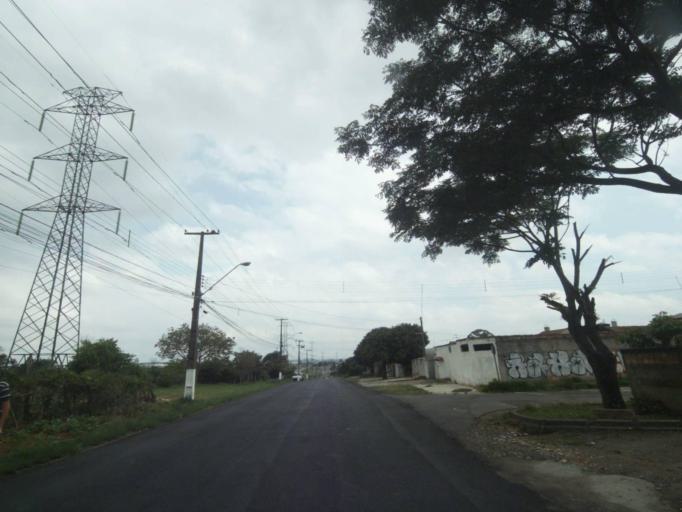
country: BR
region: Parana
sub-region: Curitiba
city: Curitiba
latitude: -25.4879
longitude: -49.3467
